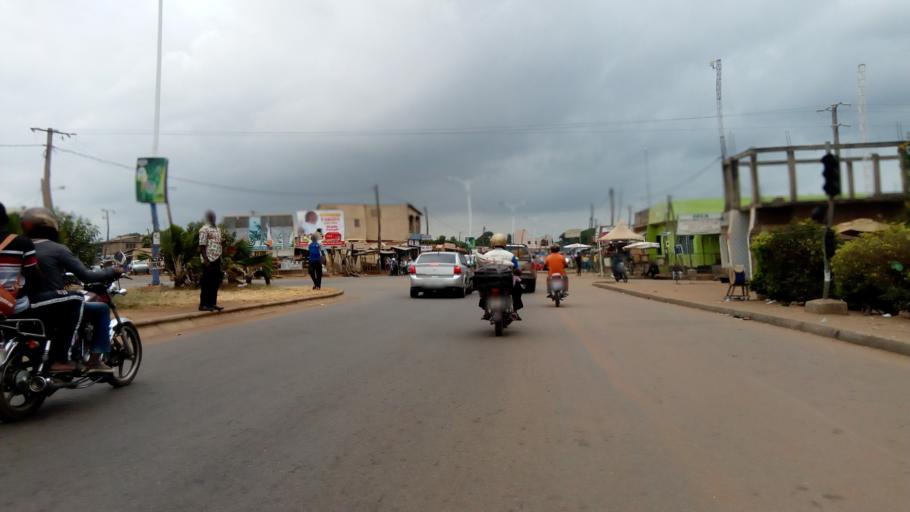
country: TG
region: Maritime
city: Lome
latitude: 6.2212
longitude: 1.2091
